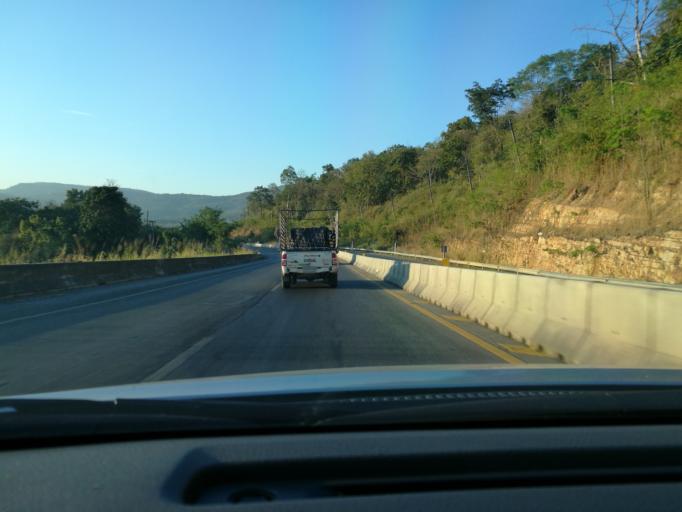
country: TH
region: Phitsanulok
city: Wang Thong
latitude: 16.8566
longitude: 100.5065
